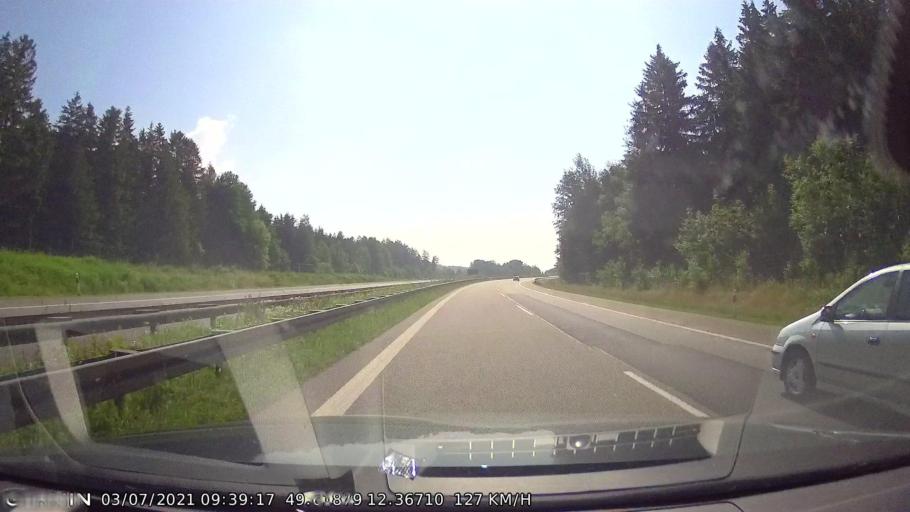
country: DE
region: Bavaria
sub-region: Upper Palatinate
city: Vohenstrauss
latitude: 49.6187
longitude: 12.3673
